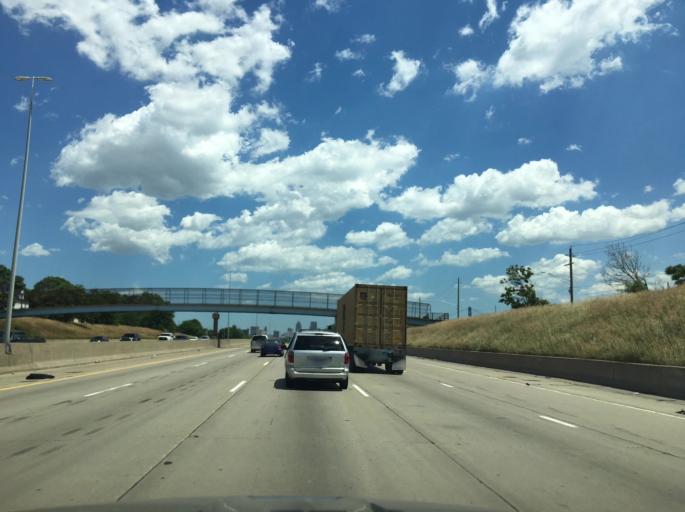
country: US
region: Michigan
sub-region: Wayne County
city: River Rouge
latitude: 42.3115
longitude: -83.0961
